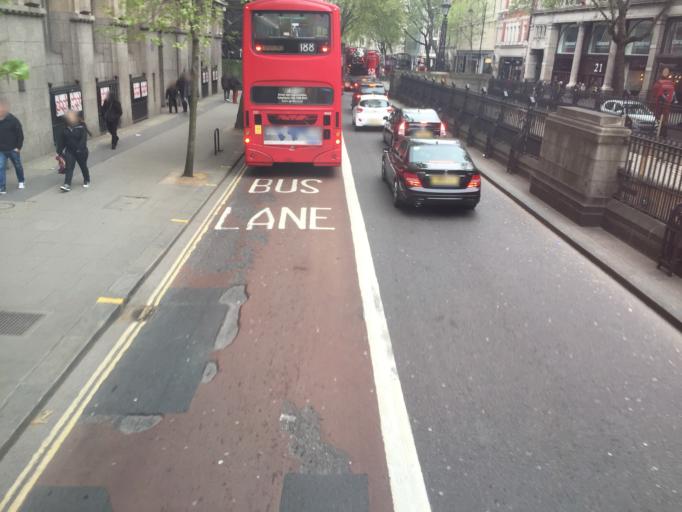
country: GB
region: England
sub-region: Greater London
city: London
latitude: 51.5187
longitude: -0.1208
